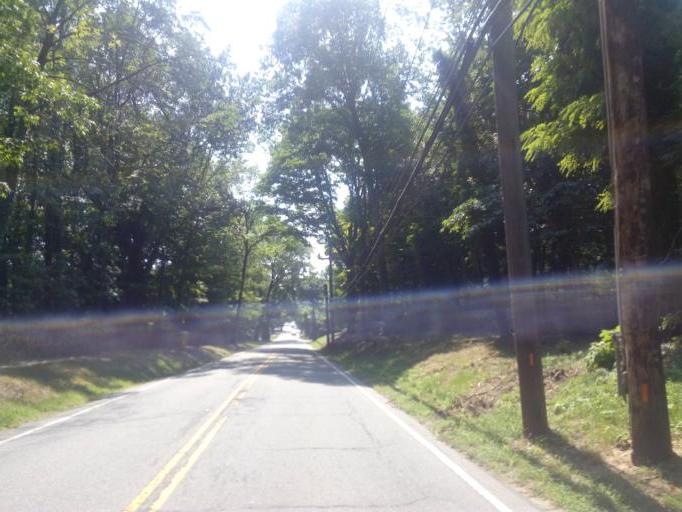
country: US
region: New York
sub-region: Nassau County
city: Glen Cove
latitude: 40.8831
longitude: -73.6306
